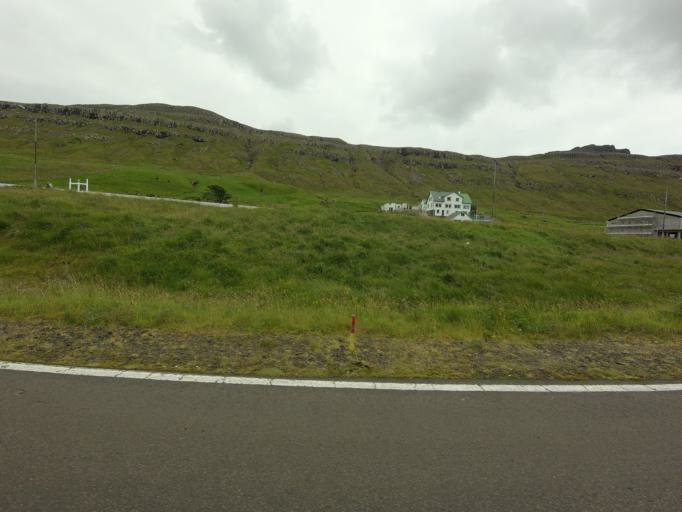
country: FO
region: Suduroy
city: Tvoroyri
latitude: 61.5486
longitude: -6.8216
